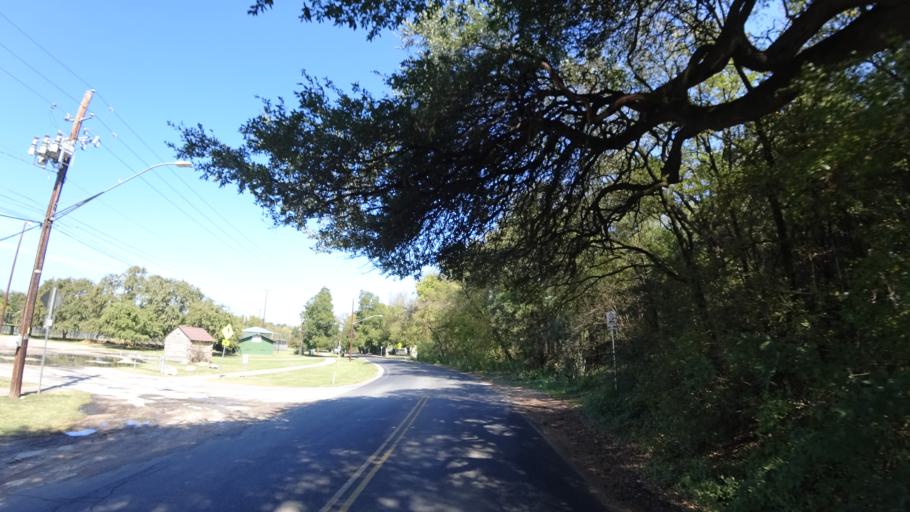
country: US
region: Texas
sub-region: Travis County
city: Austin
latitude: 30.2624
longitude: -97.7673
